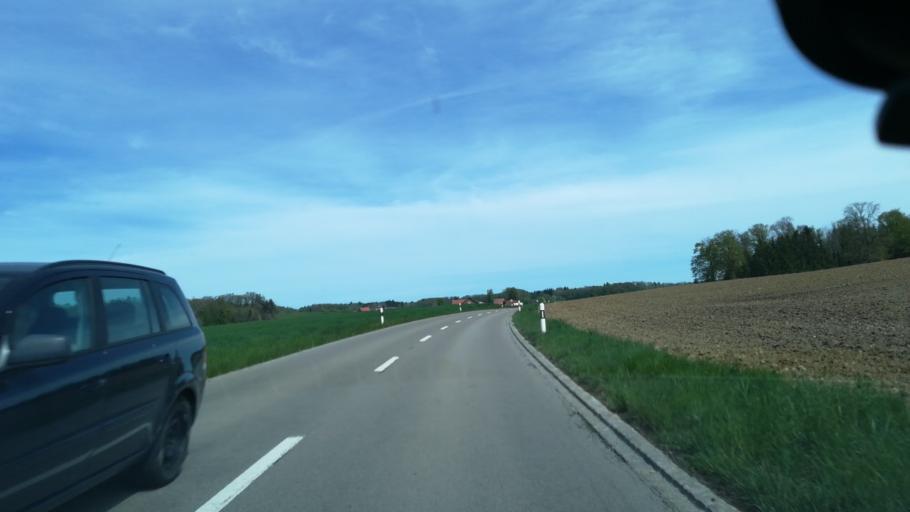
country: CH
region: Thurgau
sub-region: Weinfelden District
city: Maerstetten-Dorf
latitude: 47.6310
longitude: 9.0683
